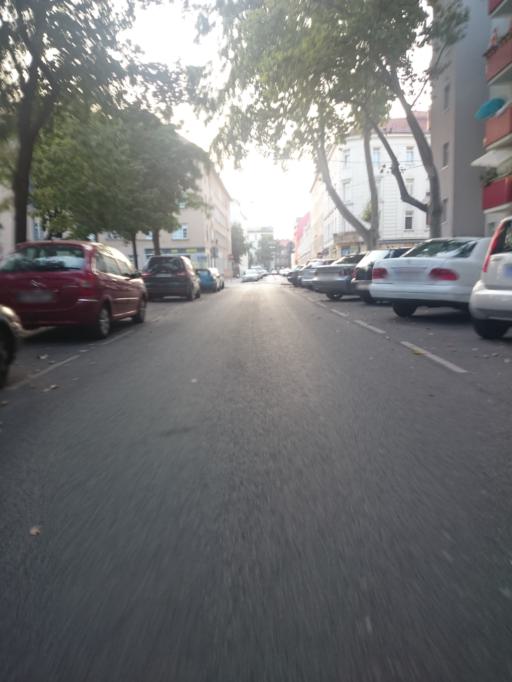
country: AT
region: Vienna
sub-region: Wien Stadt
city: Vienna
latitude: 48.2537
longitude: 16.4082
